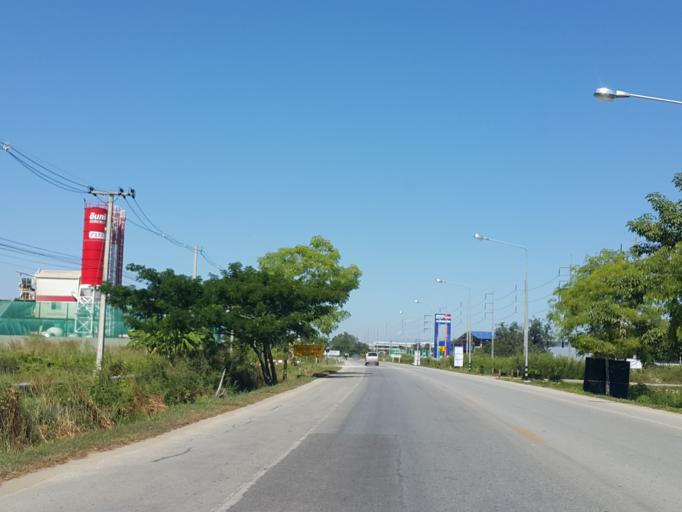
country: TH
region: Chiang Mai
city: San Sai
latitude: 18.7933
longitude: 99.0676
